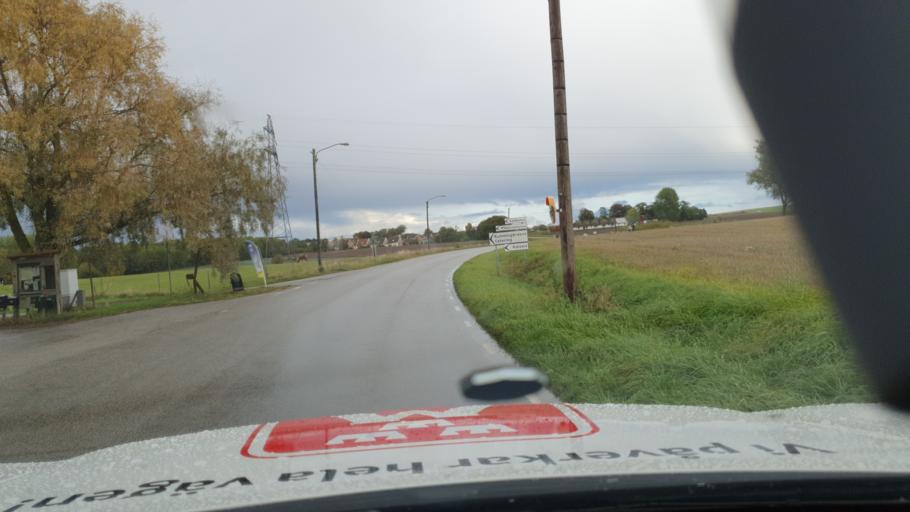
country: SE
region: Skane
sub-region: Malmo
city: Oxie
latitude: 55.5253
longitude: 13.0672
